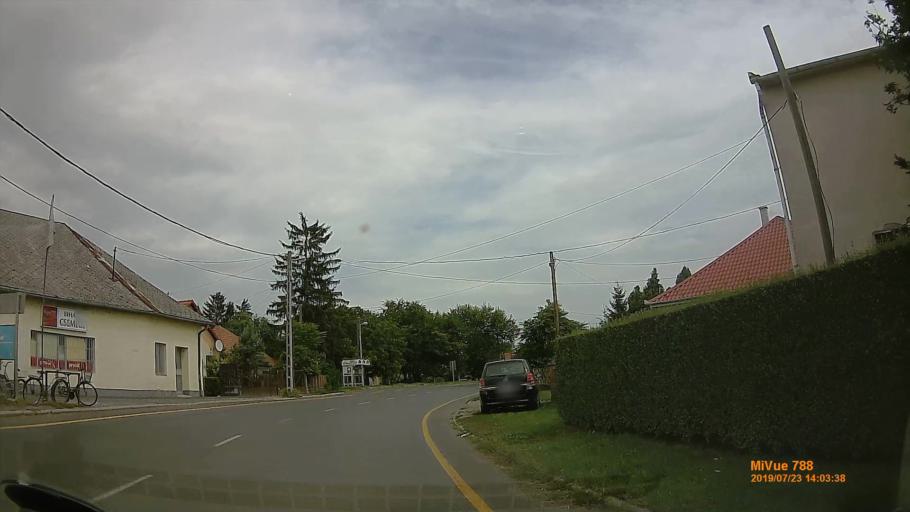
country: HU
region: Szabolcs-Szatmar-Bereg
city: Tiszavasvari
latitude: 47.9623
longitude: 21.3511
